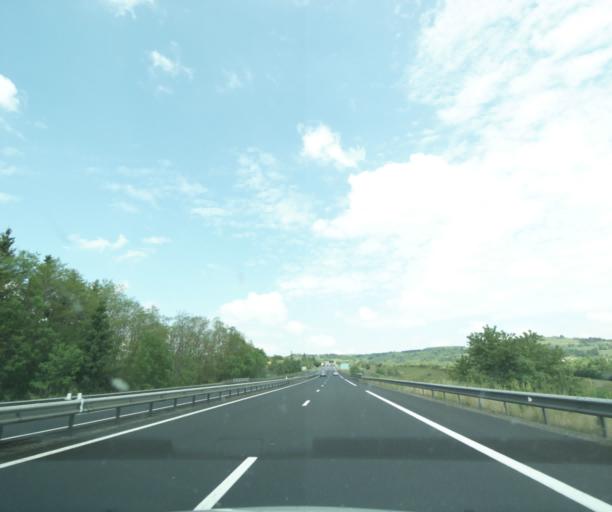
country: FR
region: Auvergne
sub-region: Departement du Cantal
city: Saint-Flour
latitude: 45.0693
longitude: 3.1135
